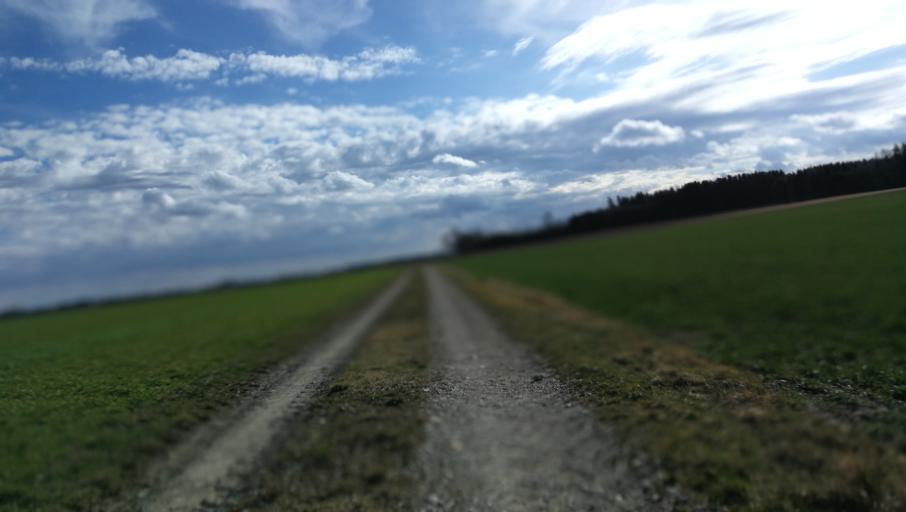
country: DE
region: Bavaria
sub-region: Upper Bavaria
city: Fuerstenfeldbruck
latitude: 48.2037
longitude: 11.2102
